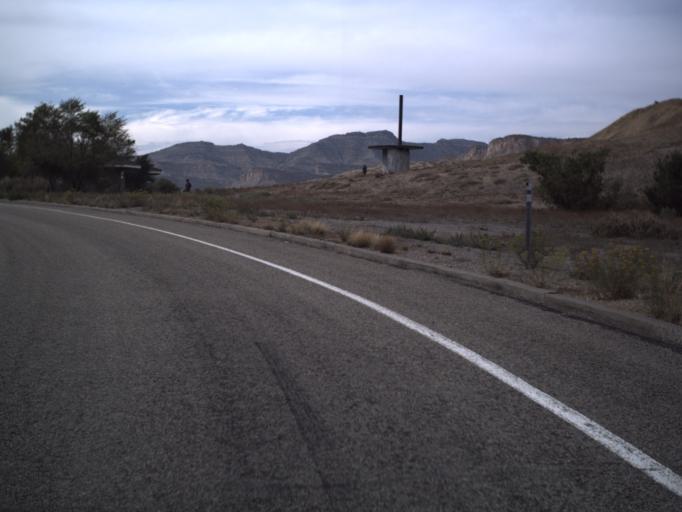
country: US
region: Utah
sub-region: Grand County
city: Moab
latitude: 38.9518
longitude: -109.6835
